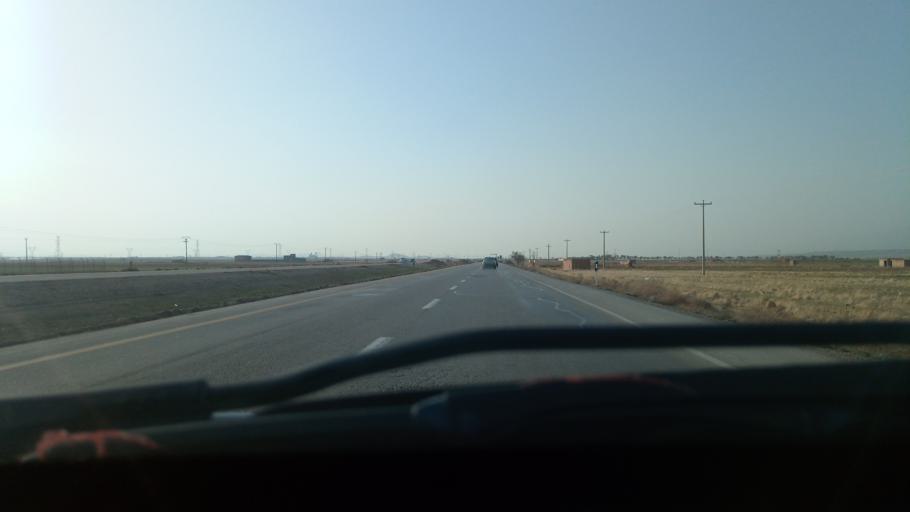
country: IR
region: Khorasan-e Shomali
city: Faruj
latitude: 37.2524
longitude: 58.1925
